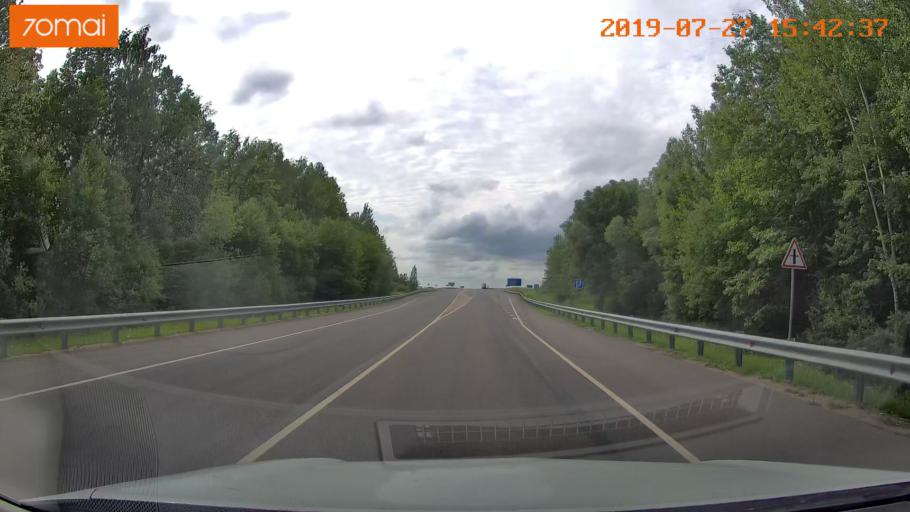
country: RU
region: Kaliningrad
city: Gusev
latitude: 54.6174
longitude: 22.2127
